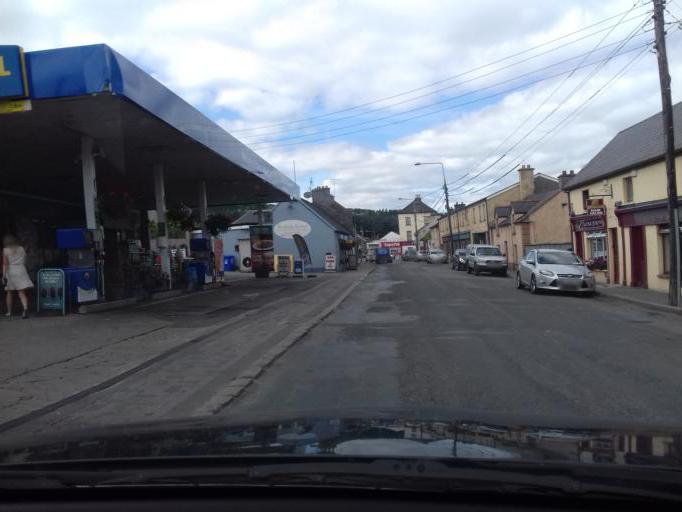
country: IE
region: Leinster
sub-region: Wicklow
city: Baltinglass
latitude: 52.9398
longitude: -6.7100
